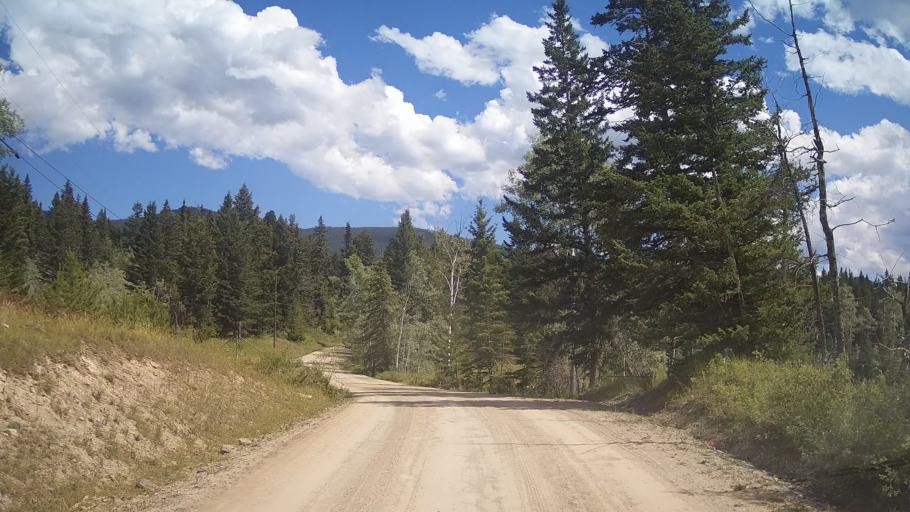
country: CA
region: British Columbia
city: Lillooet
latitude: 51.2873
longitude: -121.9719
